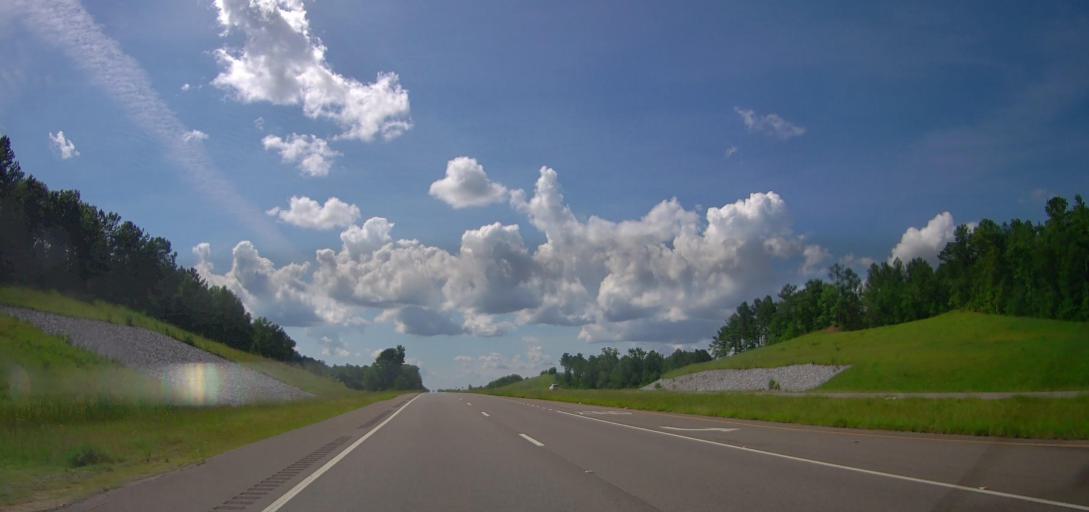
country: US
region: Alabama
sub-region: Pickens County
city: Reform
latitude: 33.3574
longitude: -87.9690
